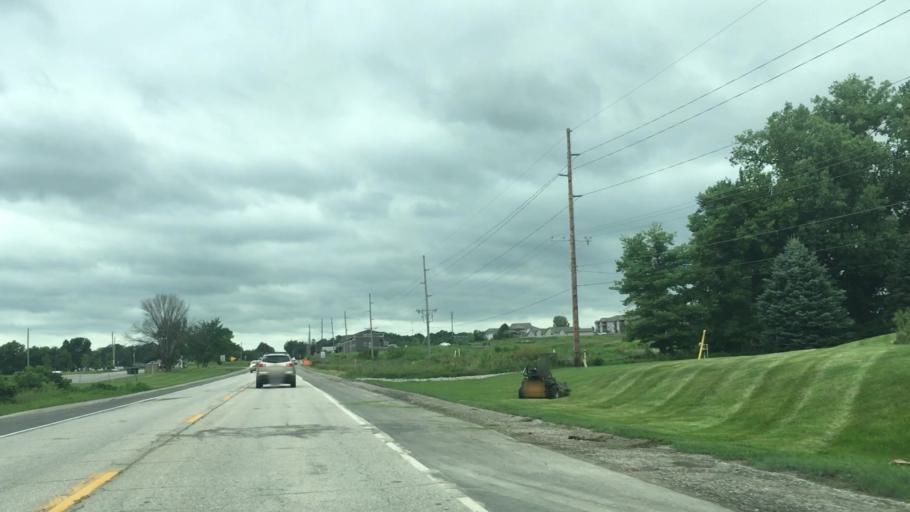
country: US
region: Iowa
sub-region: Johnson County
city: Tiffin
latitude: 41.7063
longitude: -91.6518
